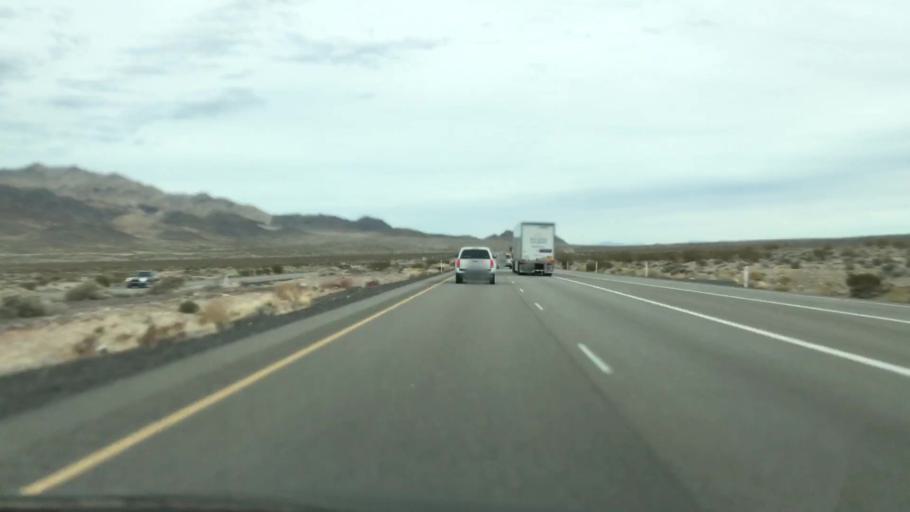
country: US
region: Nevada
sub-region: Nye County
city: Pahrump
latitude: 36.5992
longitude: -115.9913
